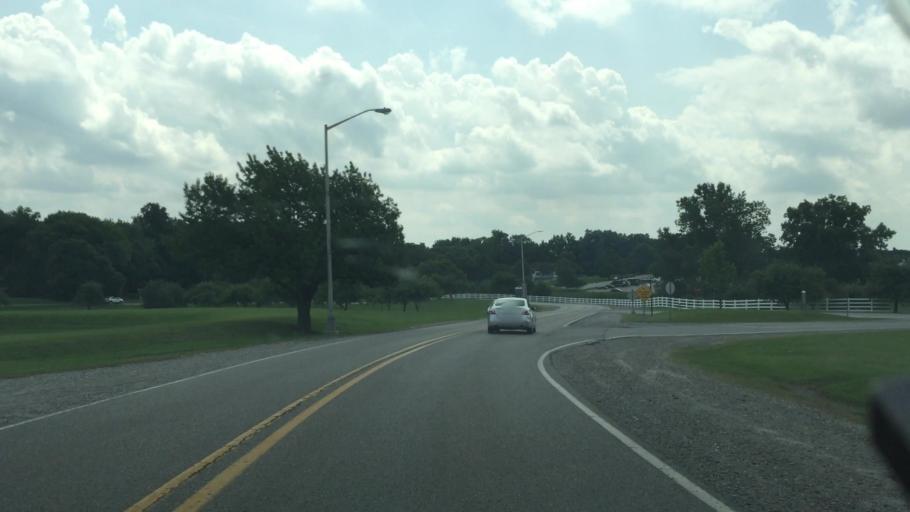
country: US
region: Michigan
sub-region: Oakland County
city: Auburn Hills
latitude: 42.6770
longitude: -83.1960
